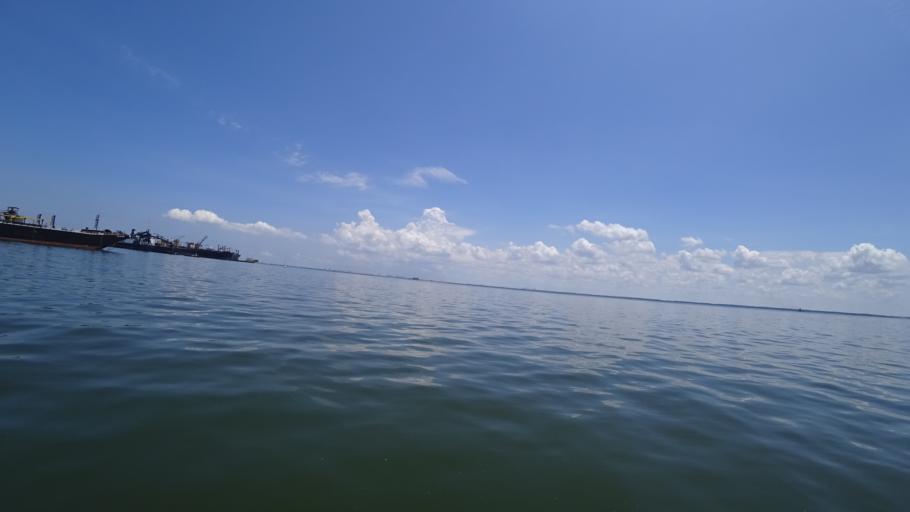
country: US
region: Virginia
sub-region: City of Newport News
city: Newport News
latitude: 36.9626
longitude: -76.4313
